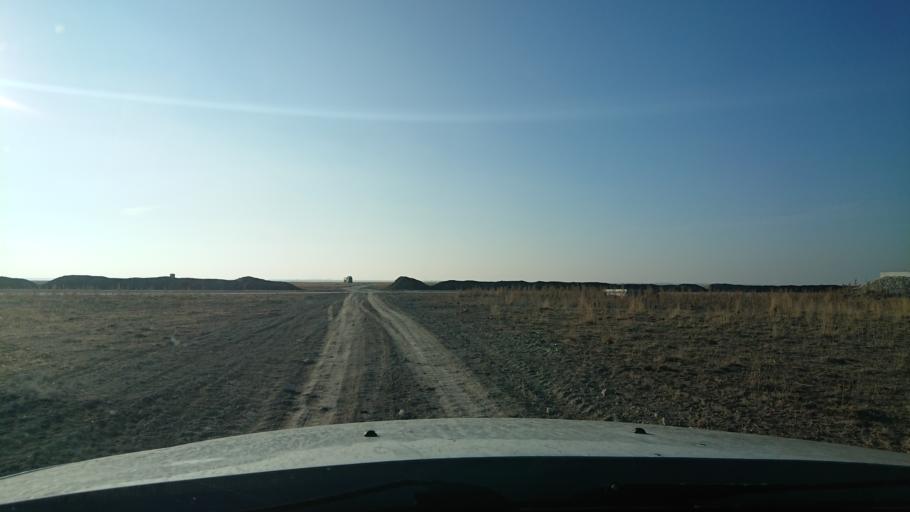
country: TR
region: Aksaray
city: Eskil
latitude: 38.3714
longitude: 33.5272
